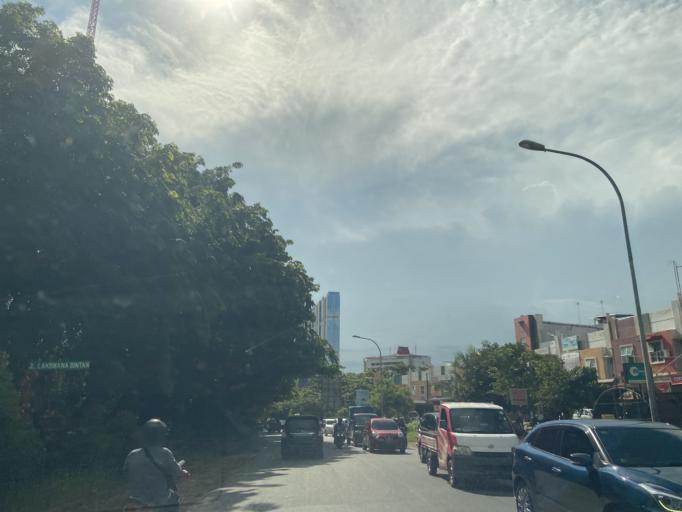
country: SG
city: Singapore
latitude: 1.1154
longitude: 104.0508
